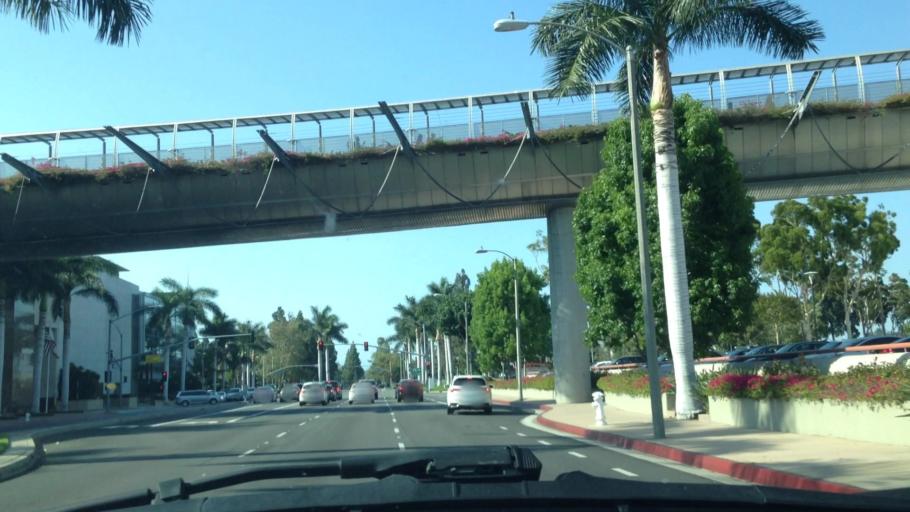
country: US
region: California
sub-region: Orange County
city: Costa Mesa
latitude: 33.6918
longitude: -117.8921
